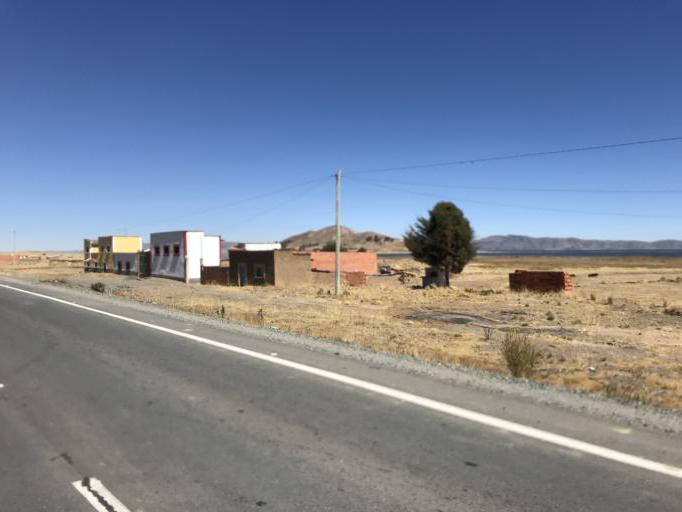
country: BO
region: La Paz
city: Huarina
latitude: -16.2124
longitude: -68.5912
